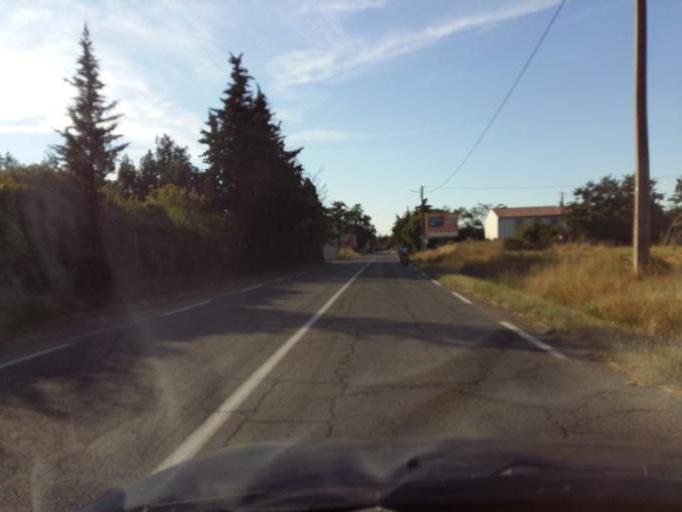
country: FR
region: Provence-Alpes-Cote d'Azur
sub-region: Departement du Vaucluse
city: Carpentras
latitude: 44.0439
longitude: 5.0613
